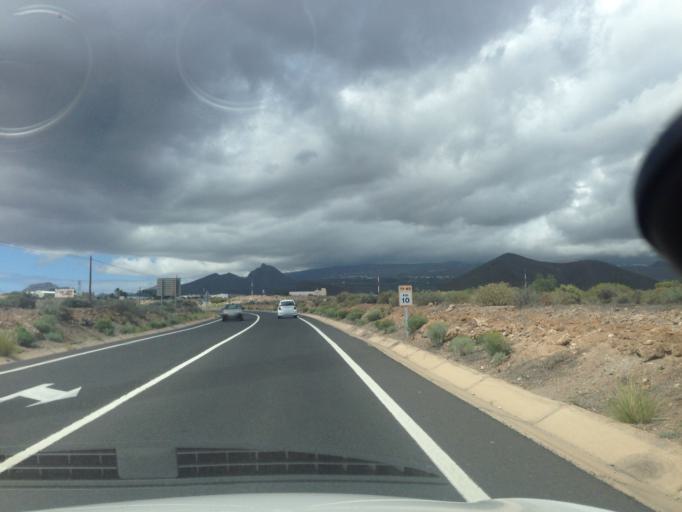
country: ES
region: Canary Islands
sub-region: Provincia de Santa Cruz de Tenerife
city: Las Rosas
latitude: 28.0430
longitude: -16.6060
